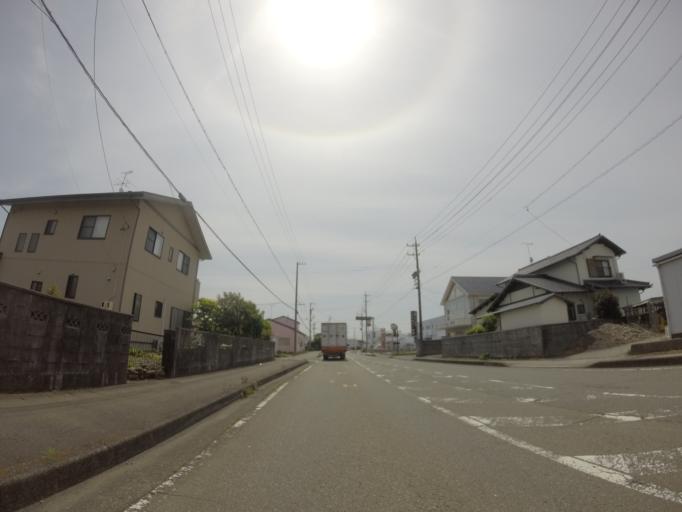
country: JP
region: Shizuoka
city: Fujieda
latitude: 34.7992
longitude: 138.2930
